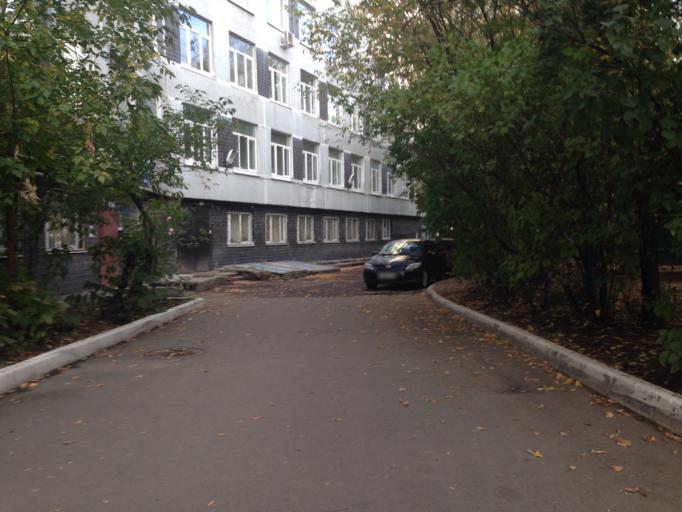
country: RU
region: Moscow
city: Mar'ina Roshcha
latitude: 55.7880
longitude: 37.6252
